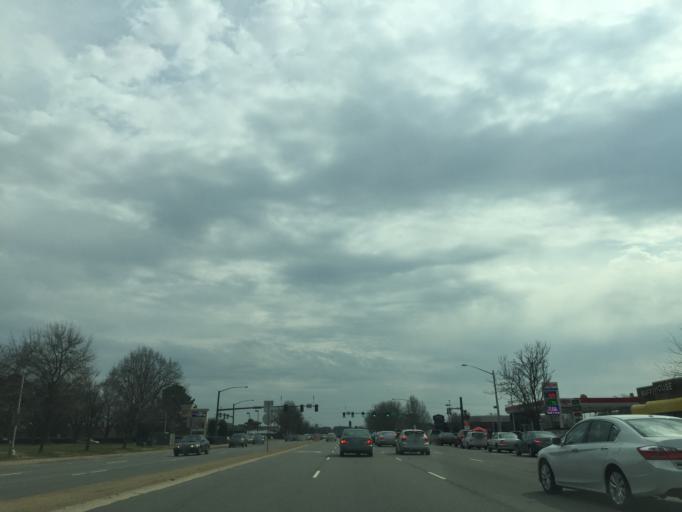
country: US
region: Virginia
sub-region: York County
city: Yorktown
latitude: 37.1137
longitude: -76.5005
